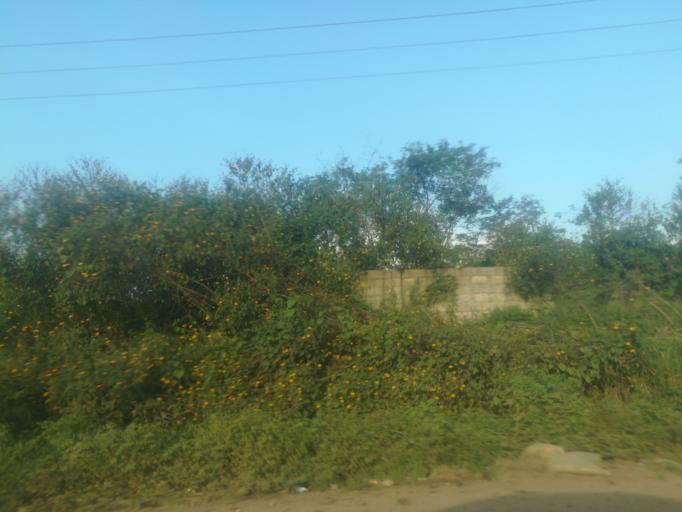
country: NG
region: Oyo
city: Moniya
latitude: 7.5430
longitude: 3.8977
